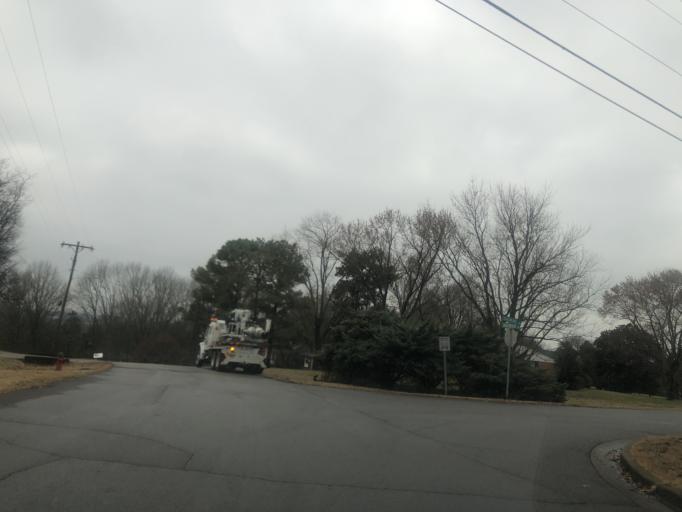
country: US
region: Tennessee
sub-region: Davidson County
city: Nashville
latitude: 36.1667
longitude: -86.6914
